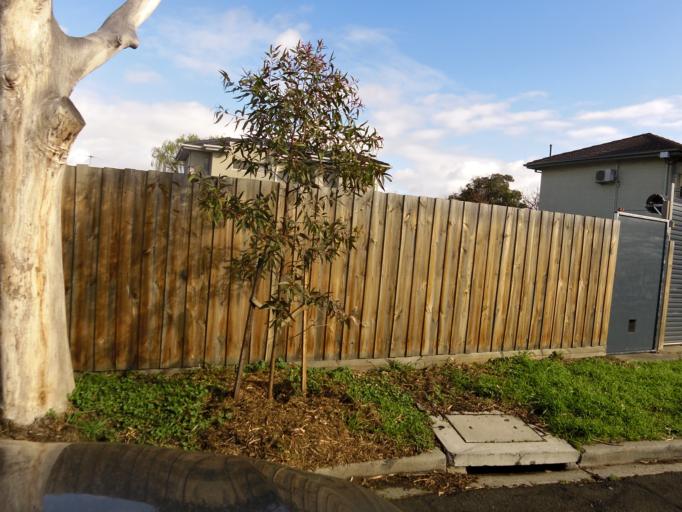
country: AU
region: Victoria
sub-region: Maribyrnong
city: Kingsville
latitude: -37.8073
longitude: 144.8678
